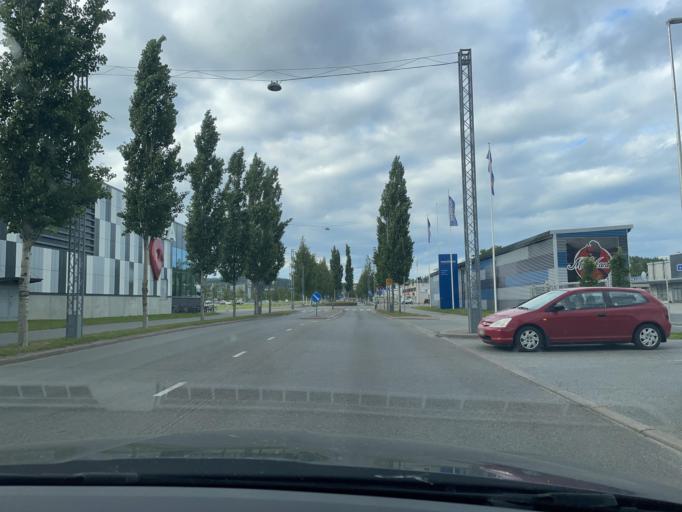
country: FI
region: Central Finland
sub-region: Jyvaeskylae
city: Jyvaeskylae
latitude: 62.2557
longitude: 25.7773
